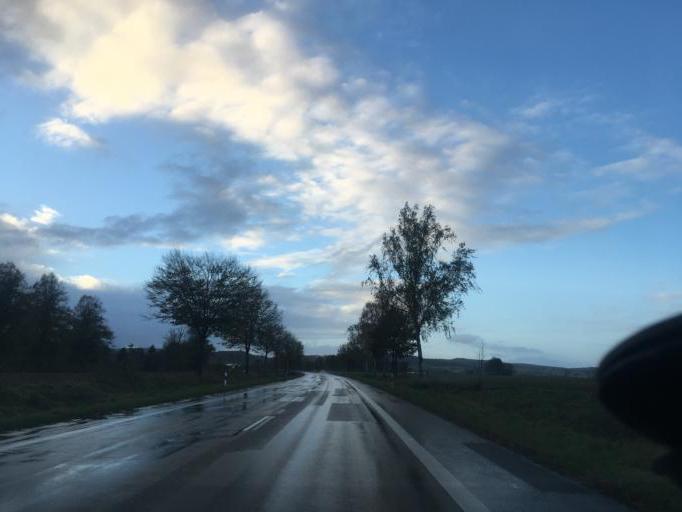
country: DE
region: Lower Saxony
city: Norten-Hardenberg
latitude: 51.6373
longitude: 9.8865
